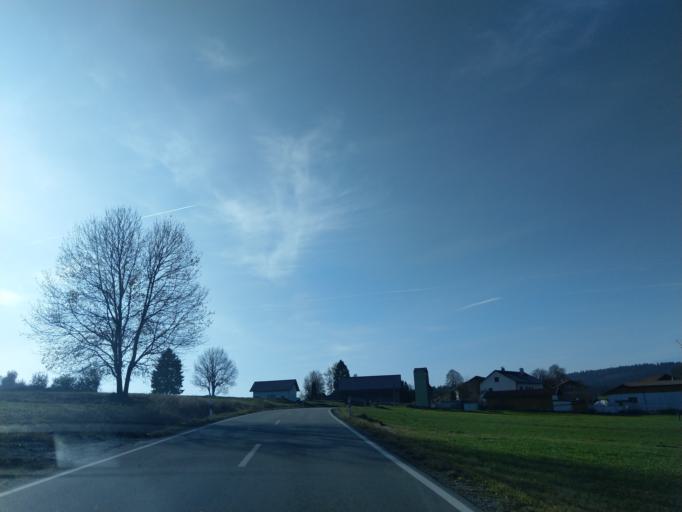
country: DE
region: Bavaria
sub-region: Lower Bavaria
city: Lalling
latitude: 48.8930
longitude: 13.1322
